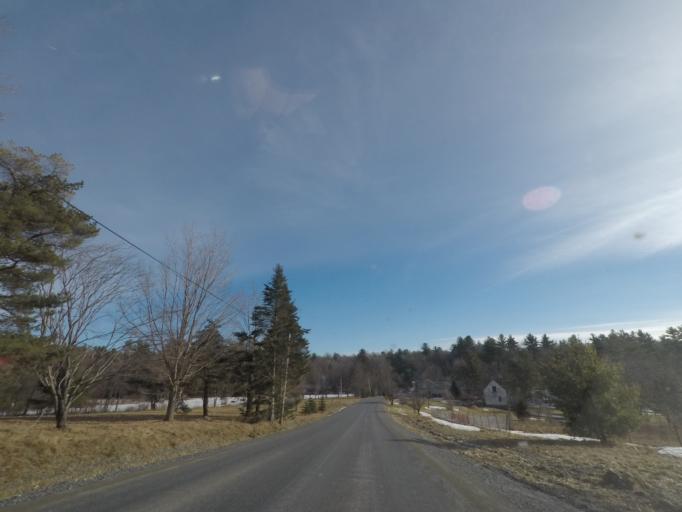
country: US
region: New York
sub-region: Rensselaer County
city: Hoosick Falls
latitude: 42.7639
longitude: -73.4256
